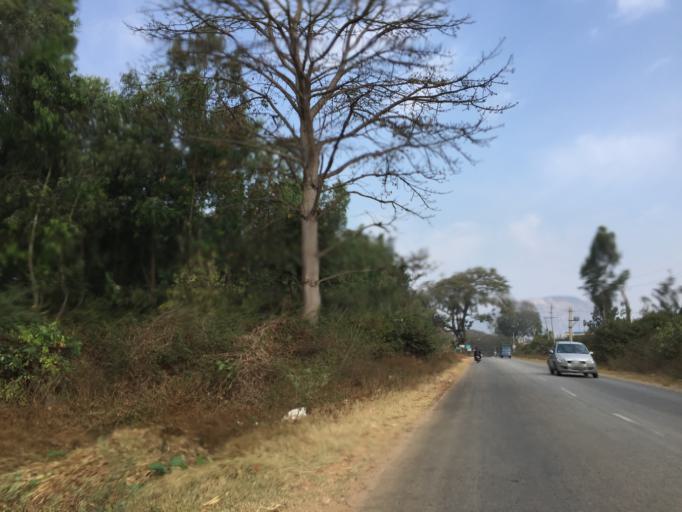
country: IN
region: Karnataka
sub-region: Bangalore Rural
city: Devanhalli
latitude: 13.3243
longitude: 77.6929
